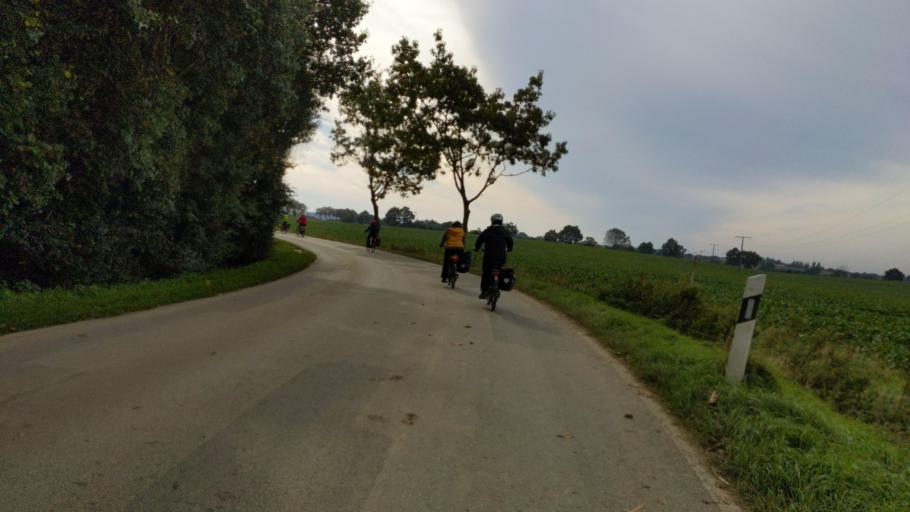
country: DE
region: Schleswig-Holstein
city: Rehhorst
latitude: 53.8912
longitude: 10.4759
